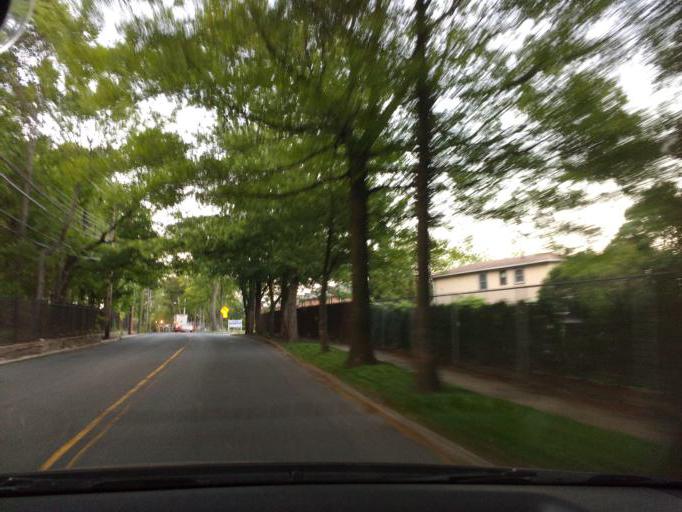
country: US
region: New York
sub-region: Richmond County
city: Staten Island
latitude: 40.5581
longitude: -74.1372
